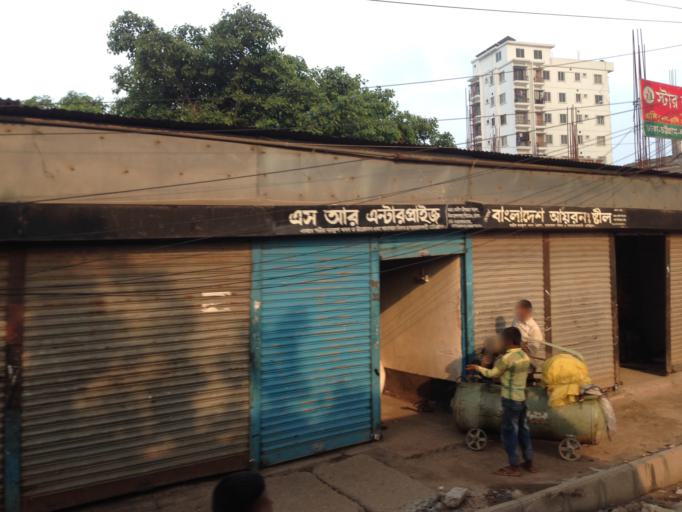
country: BD
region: Dhaka
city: Paltan
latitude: 23.7304
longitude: 90.4286
